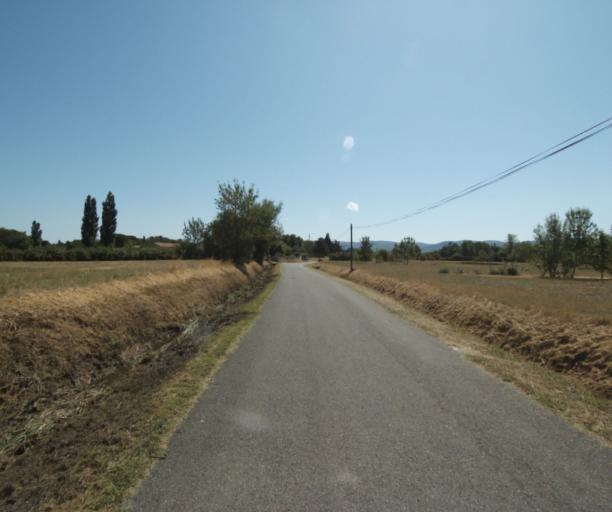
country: FR
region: Midi-Pyrenees
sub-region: Departement de la Haute-Garonne
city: Revel
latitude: 43.4732
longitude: 1.9881
